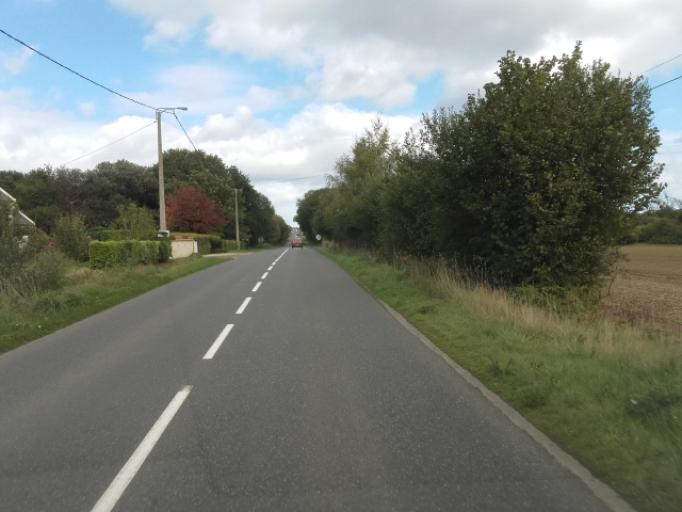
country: FR
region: Brittany
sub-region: Departement des Cotes-d'Armor
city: Plouha
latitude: 48.6692
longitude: -2.9445
